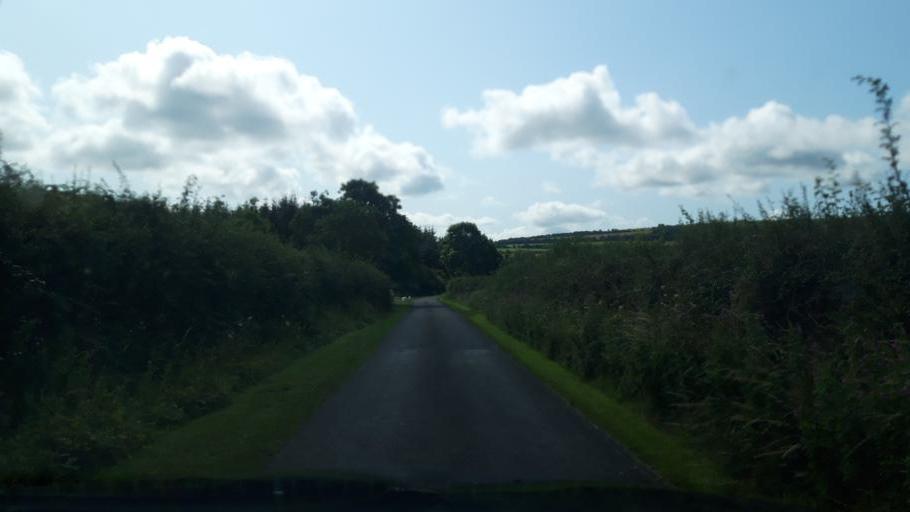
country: IE
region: Leinster
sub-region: Kilkenny
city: Graiguenamanagh
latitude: 52.5822
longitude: -6.9909
